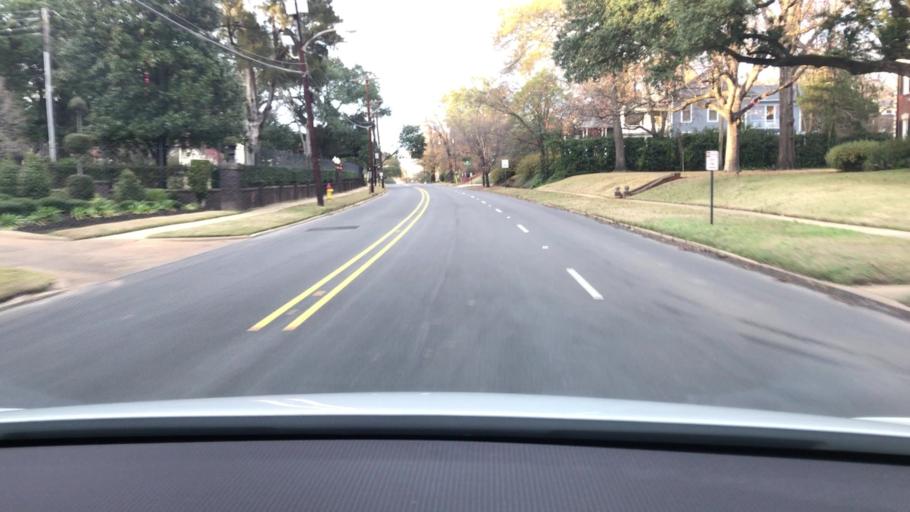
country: US
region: Louisiana
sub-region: Bossier Parish
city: Bossier City
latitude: 32.4867
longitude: -93.7497
